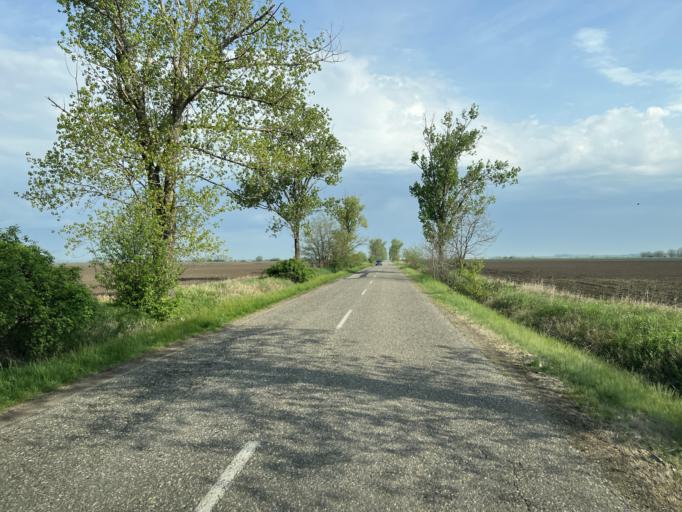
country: HU
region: Pest
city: Tapioszentmarton
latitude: 47.2747
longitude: 19.7674
